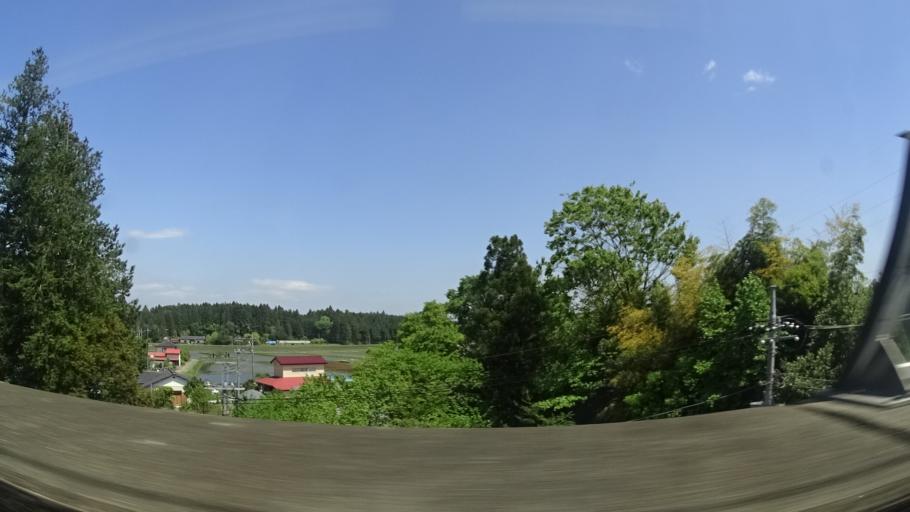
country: JP
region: Tochigi
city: Yaita
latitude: 36.7477
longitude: 139.9377
